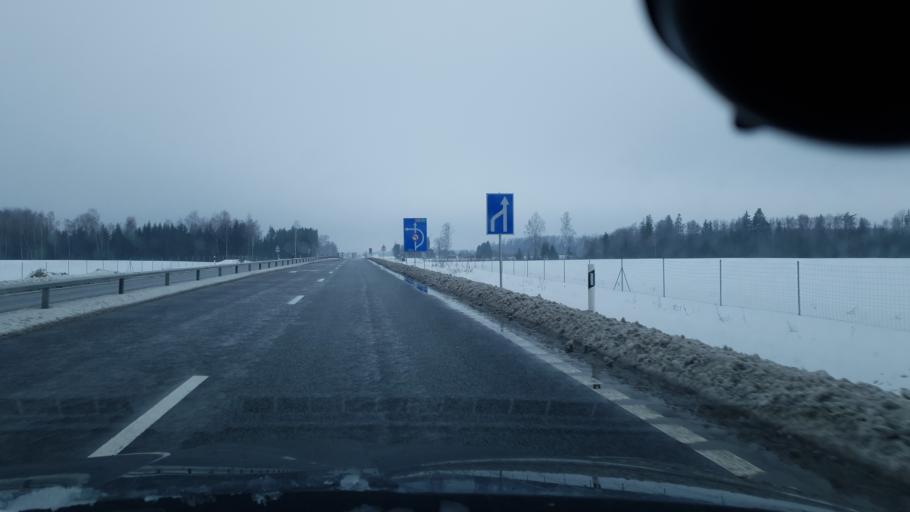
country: EE
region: Jogevamaa
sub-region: Tabivere vald
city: Tabivere
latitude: 58.4370
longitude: 26.4649
